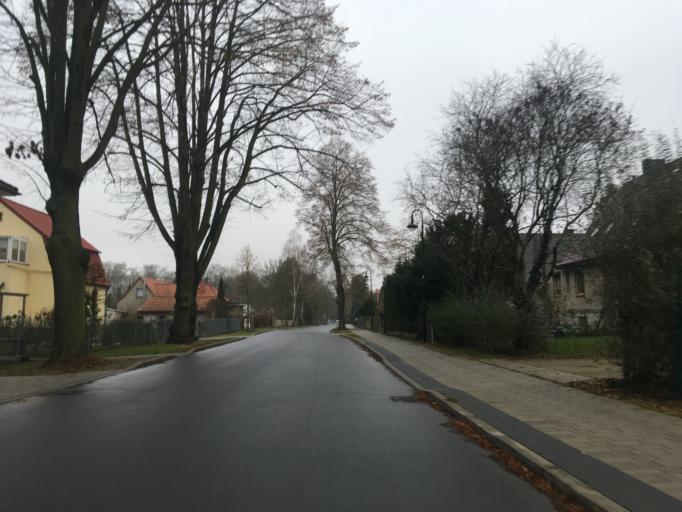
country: DE
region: Berlin
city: Buch
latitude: 52.6283
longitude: 13.5153
